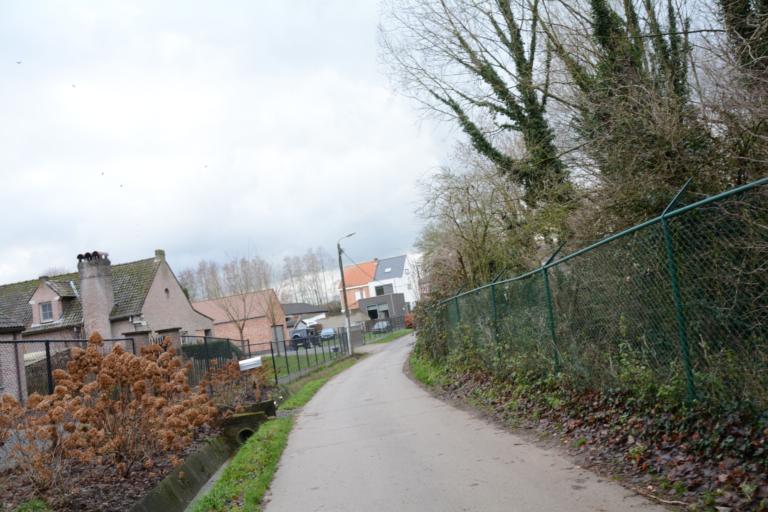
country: BE
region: Flanders
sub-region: Provincie Vlaams-Brabant
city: Merchtem
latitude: 50.9400
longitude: 4.2512
